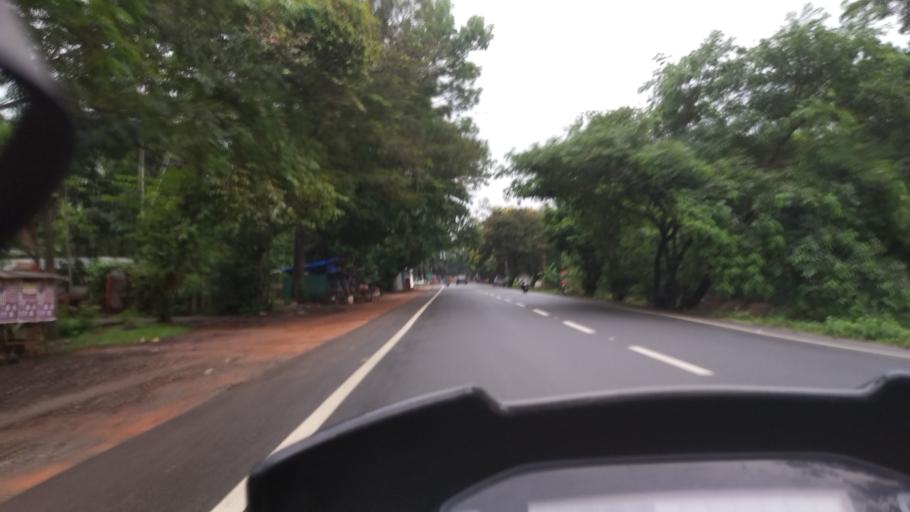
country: IN
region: Kerala
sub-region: Alappuzha
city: Mavelikara
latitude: 9.3047
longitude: 76.4324
